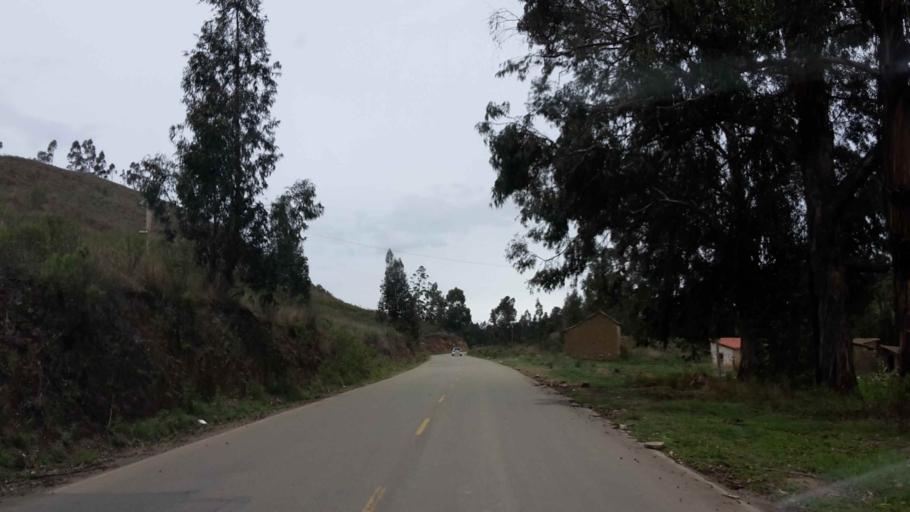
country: BO
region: Cochabamba
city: Totora
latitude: -17.7227
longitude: -65.1981
